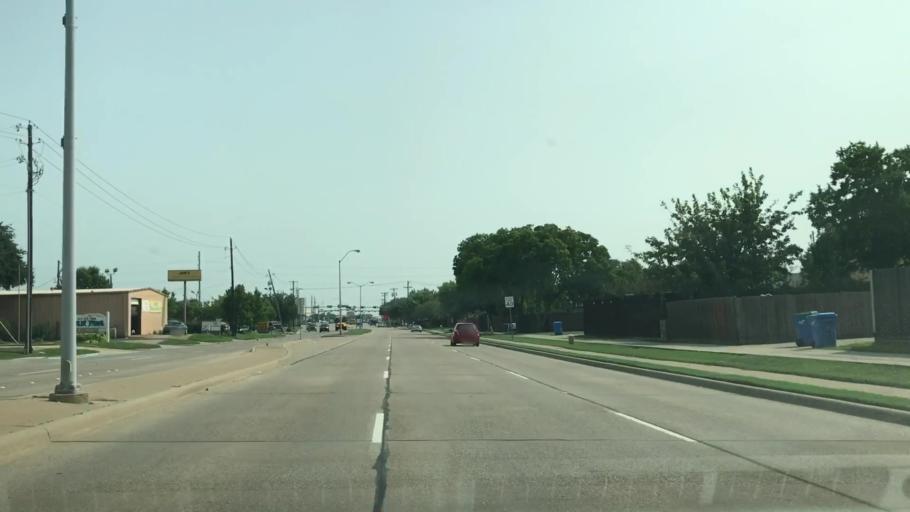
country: US
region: Texas
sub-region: Dallas County
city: Rowlett
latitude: 32.9119
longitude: -96.5696
